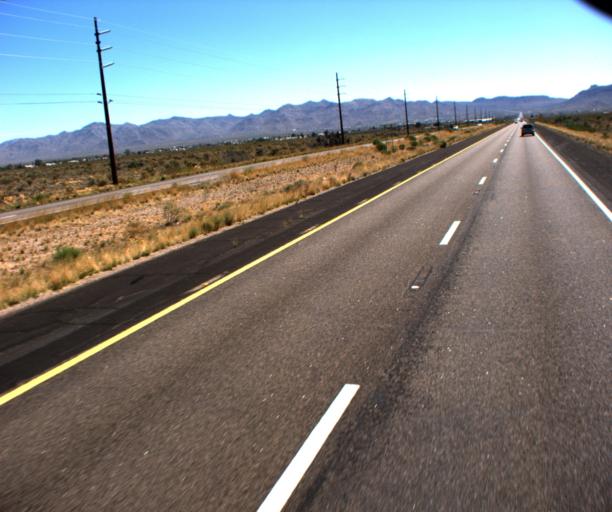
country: US
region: Arizona
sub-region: Mohave County
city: Golden Valley
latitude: 35.2228
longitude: -114.2338
